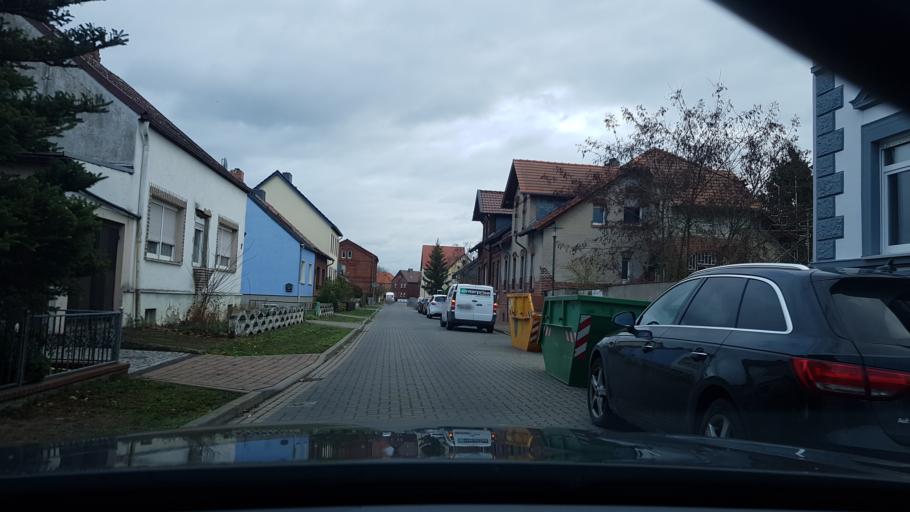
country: DE
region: Saxony-Anhalt
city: Oebisfelde
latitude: 52.4386
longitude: 10.9880
